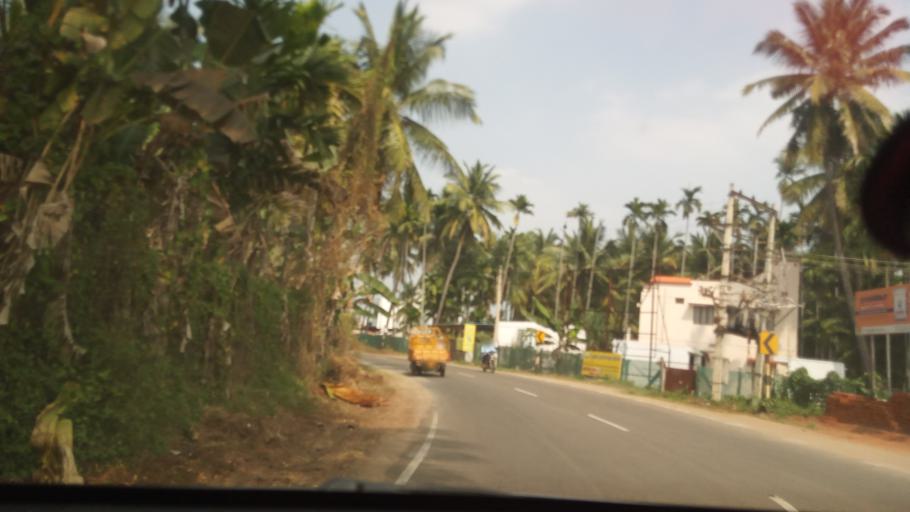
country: IN
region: Tamil Nadu
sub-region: Coimbatore
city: Perur
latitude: 11.0026
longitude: 76.8600
